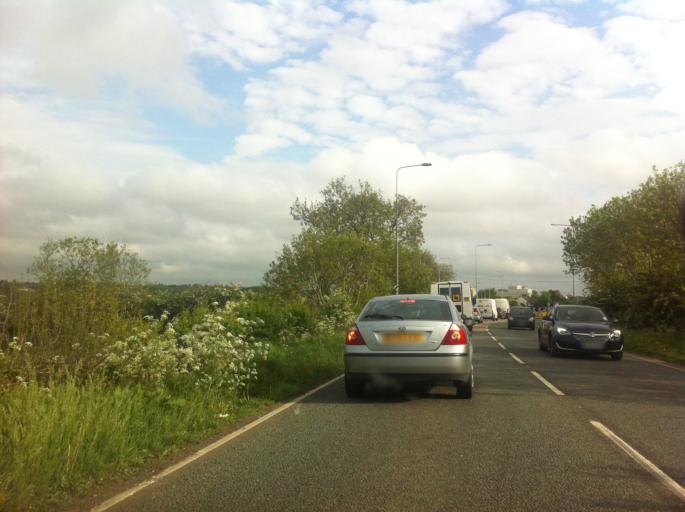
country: GB
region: England
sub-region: Northamptonshire
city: Wellingborough
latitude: 52.2814
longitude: -0.6769
